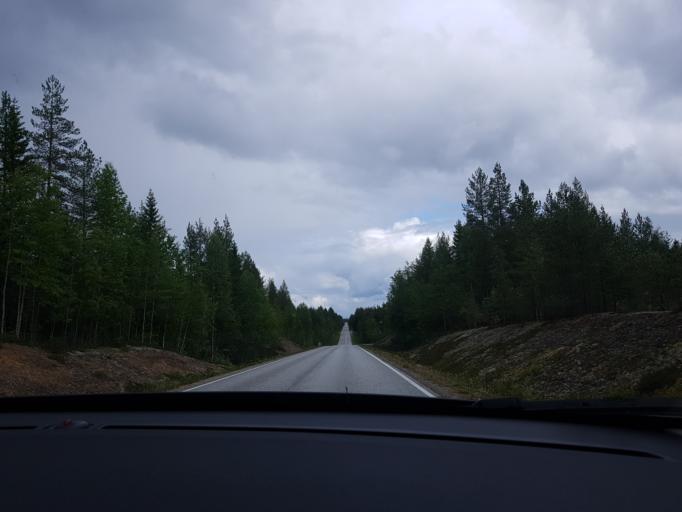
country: FI
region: Kainuu
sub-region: Kehys-Kainuu
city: Kuhmo
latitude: 64.3391
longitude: 29.4849
